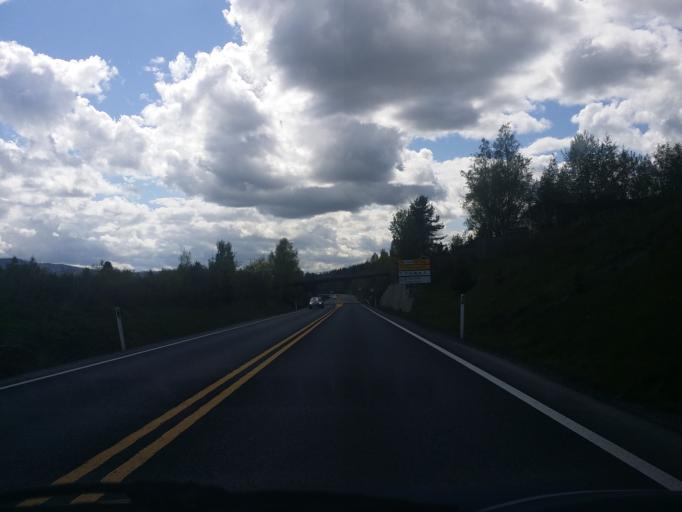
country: NO
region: Buskerud
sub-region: Modum
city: Vikersund
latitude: 59.9677
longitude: 9.9848
